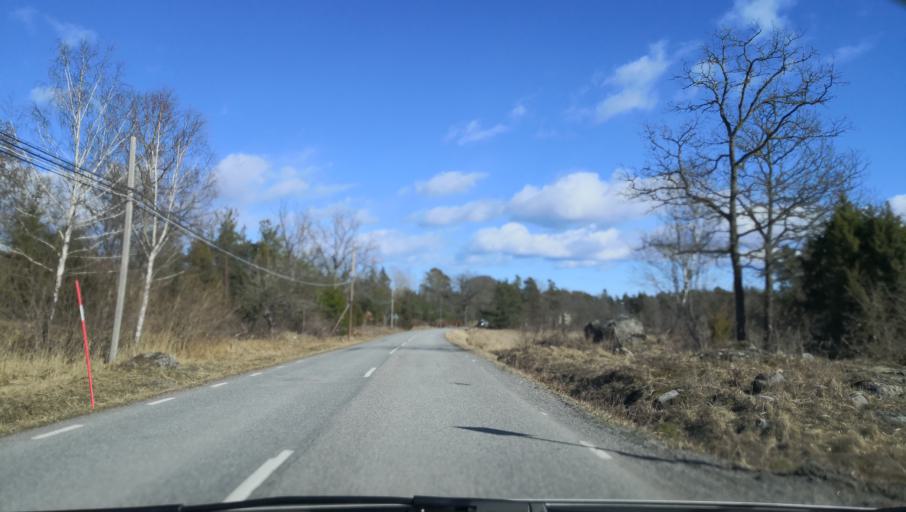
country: SE
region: Stockholm
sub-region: Varmdo Kommun
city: Holo
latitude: 59.3559
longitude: 18.6078
